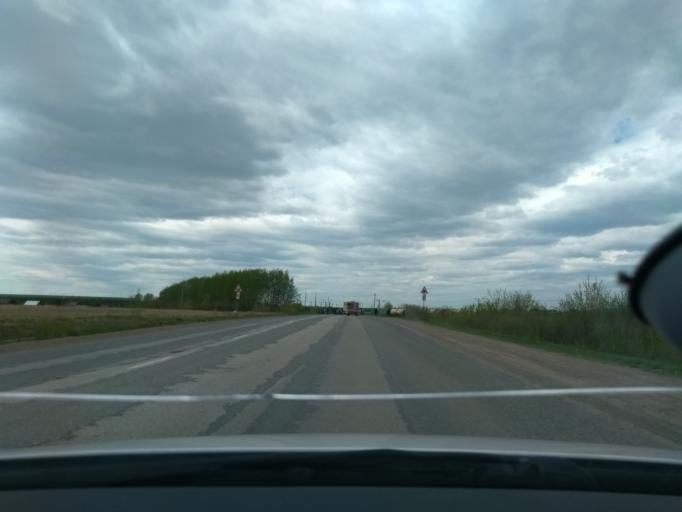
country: RU
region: Perm
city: Lobanovo
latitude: 57.8759
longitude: 56.2752
